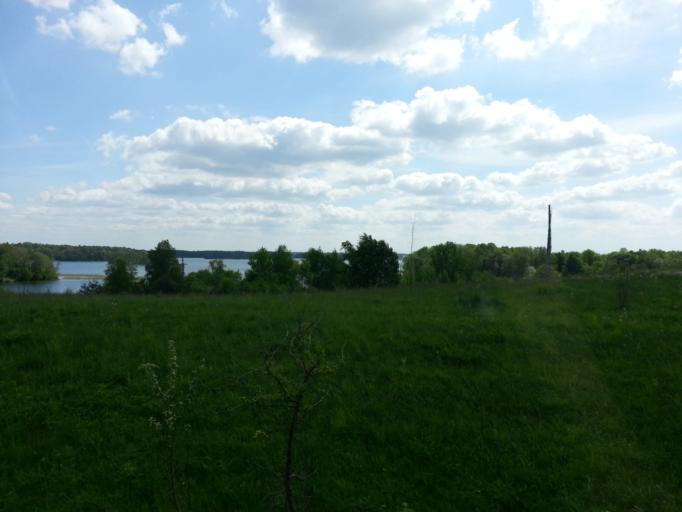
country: LT
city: Trakai
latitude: 54.6732
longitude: 24.9321
